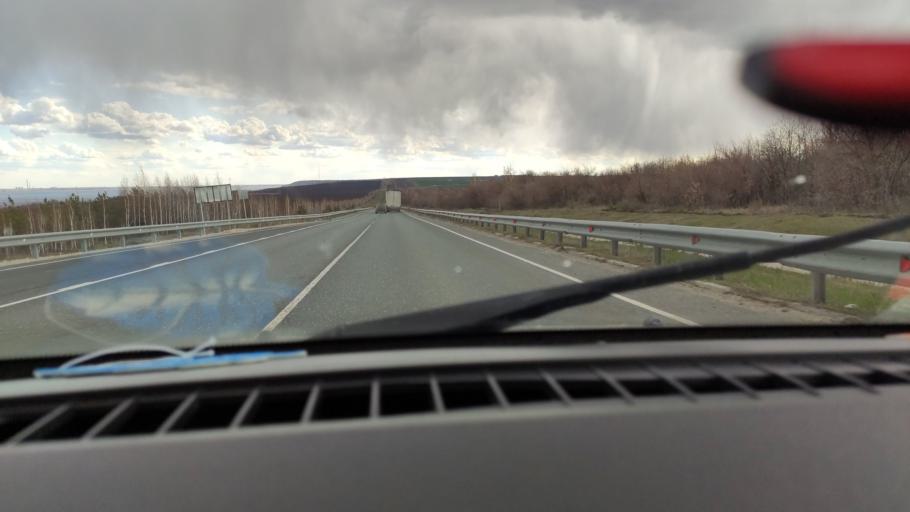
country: RU
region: Saratov
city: Balakovo
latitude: 52.1542
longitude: 47.8144
